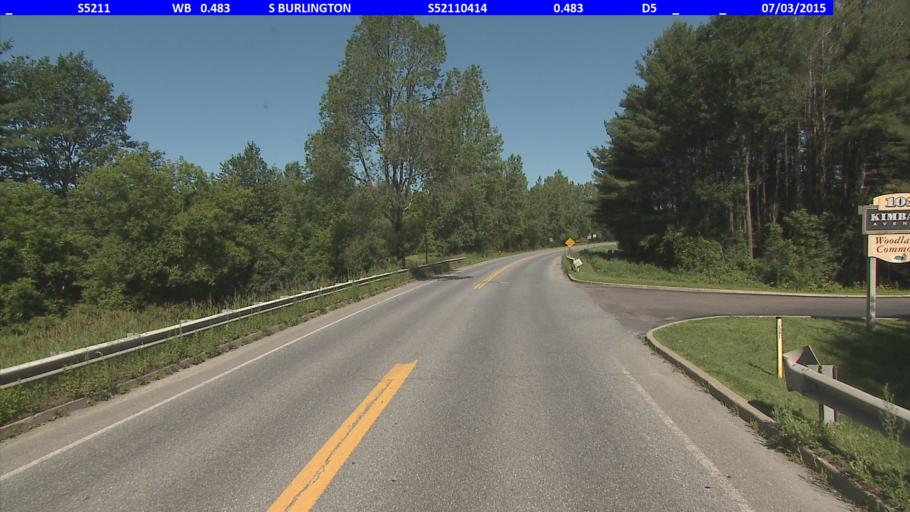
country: US
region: Vermont
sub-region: Chittenden County
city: South Burlington
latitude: 44.4549
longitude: -73.1485
